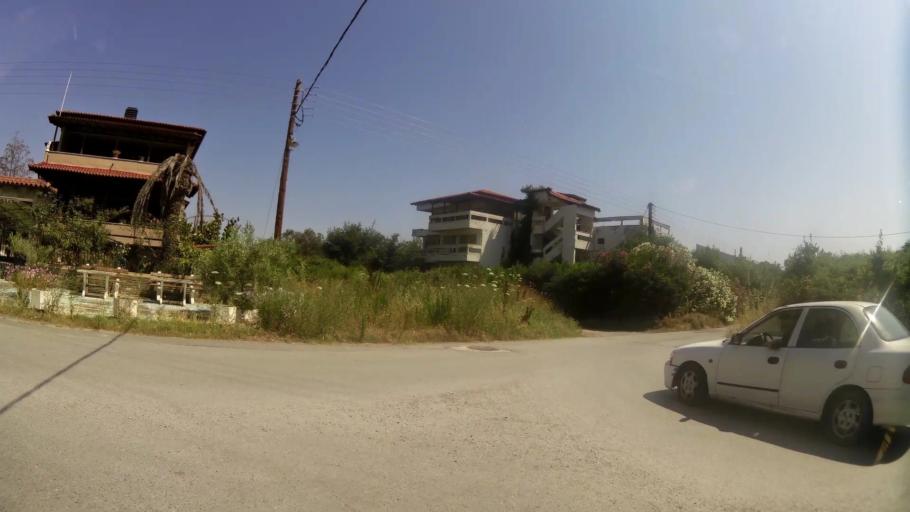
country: GR
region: Central Macedonia
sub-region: Nomos Thessalonikis
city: Neoi Epivates
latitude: 40.5006
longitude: 22.8981
